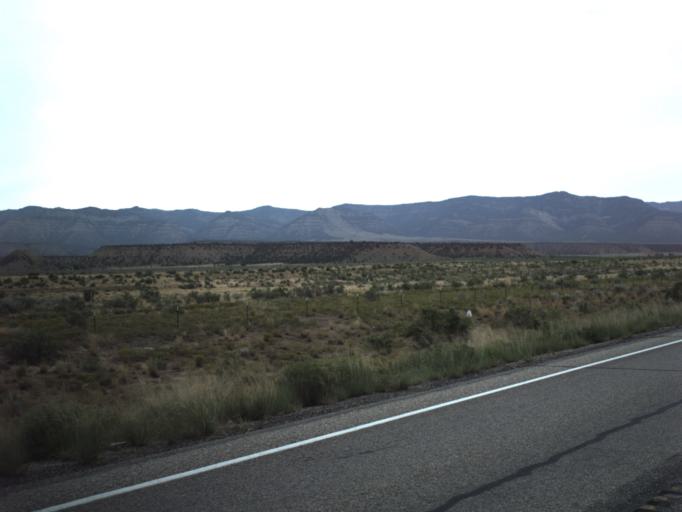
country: US
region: Utah
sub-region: Carbon County
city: East Carbon City
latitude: 39.5348
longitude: -110.5148
